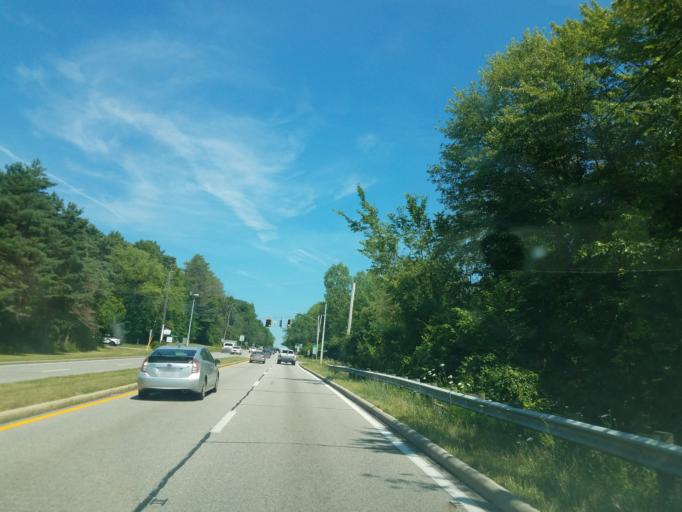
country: US
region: Ohio
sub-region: Cuyahoga County
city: Gates Mills
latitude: 41.5226
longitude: -81.3919
